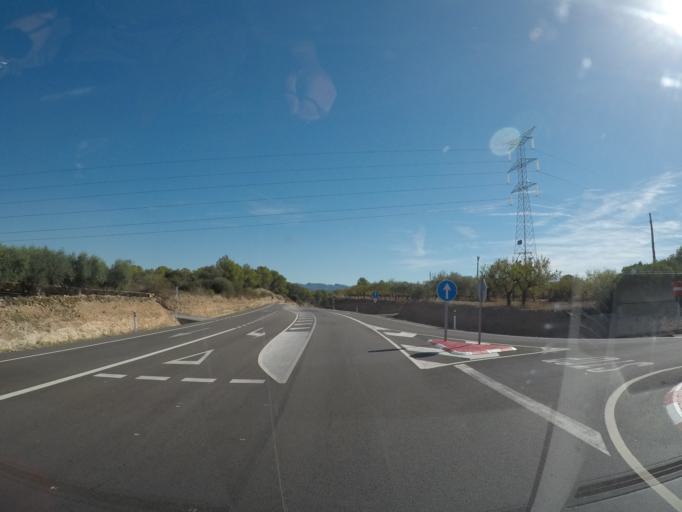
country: ES
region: Catalonia
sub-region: Provincia de Tarragona
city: Garcia
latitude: 41.1085
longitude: 0.6885
